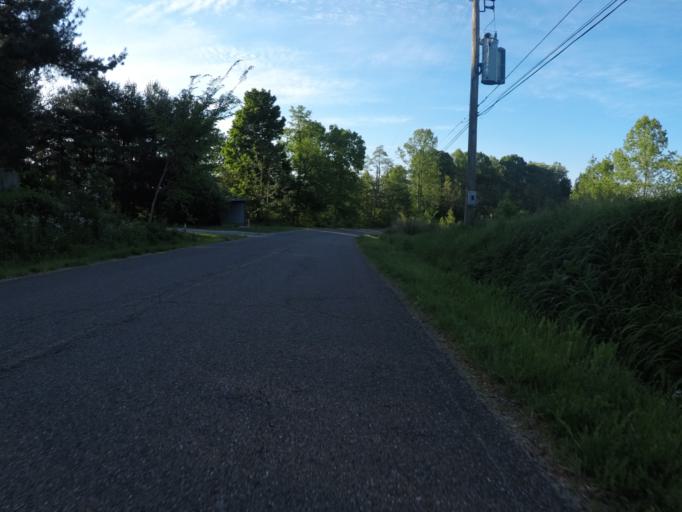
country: US
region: West Virginia
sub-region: Cabell County
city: Huntington
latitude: 38.5458
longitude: -82.4312
